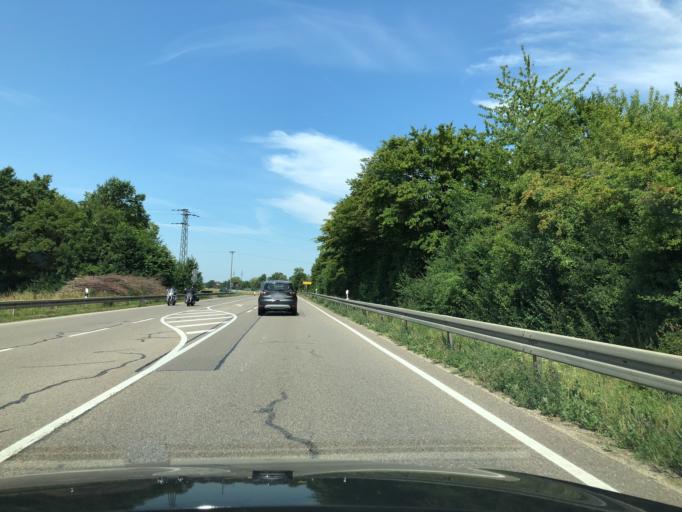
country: DE
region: Bavaria
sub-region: Upper Bavaria
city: Manching
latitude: 48.7154
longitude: 11.4652
